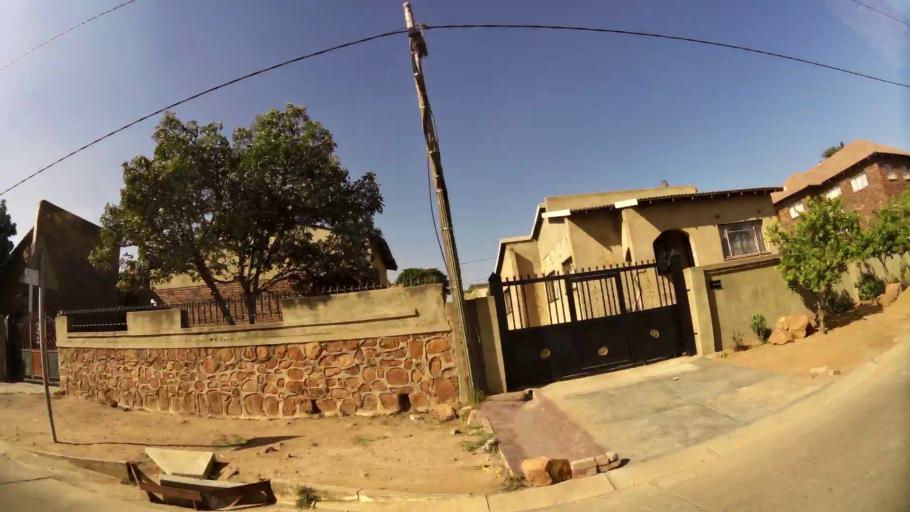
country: ZA
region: Gauteng
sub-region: City of Tshwane Metropolitan Municipality
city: Mabopane
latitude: -25.5327
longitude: 28.0878
